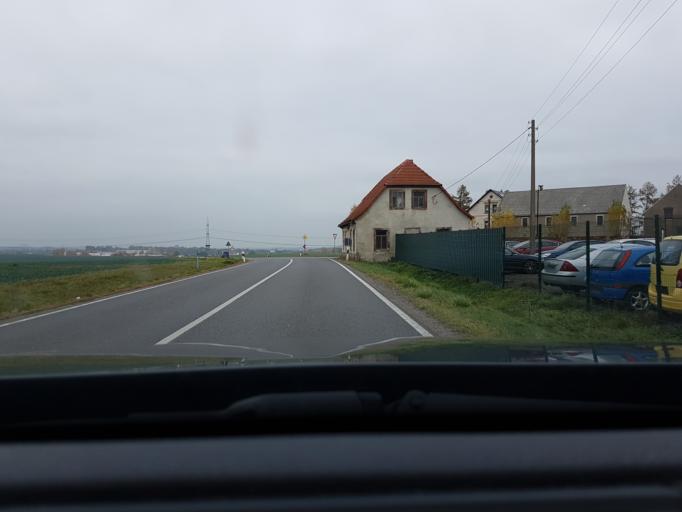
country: DE
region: Saxony
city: Altmittweida
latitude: 50.9545
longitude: 12.9738
